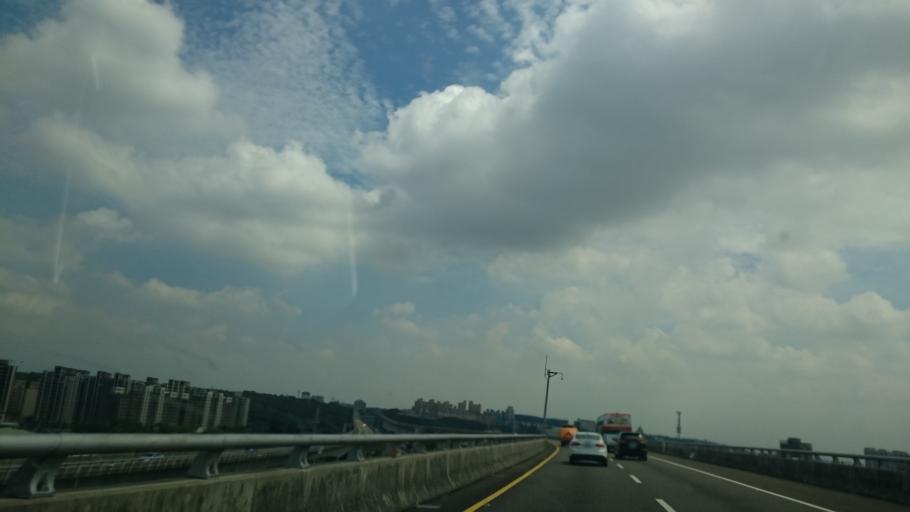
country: TW
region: Taiwan
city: Daxi
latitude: 24.9053
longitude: 121.1627
